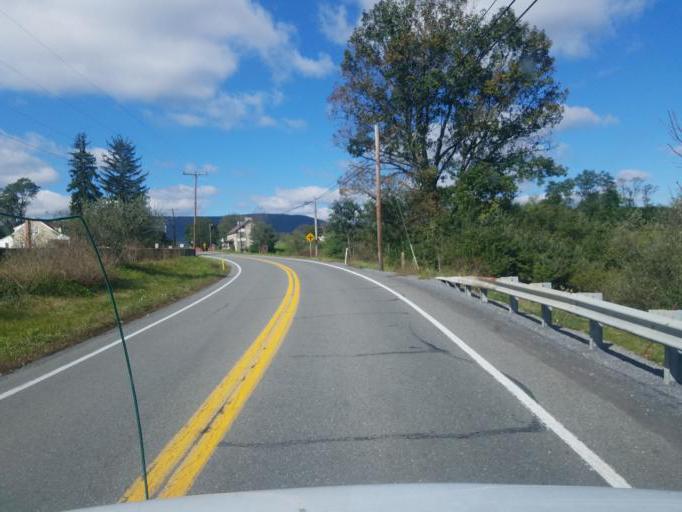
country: US
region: Pennsylvania
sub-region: Fulton County
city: McConnellsburg
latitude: 39.9924
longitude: -78.0831
